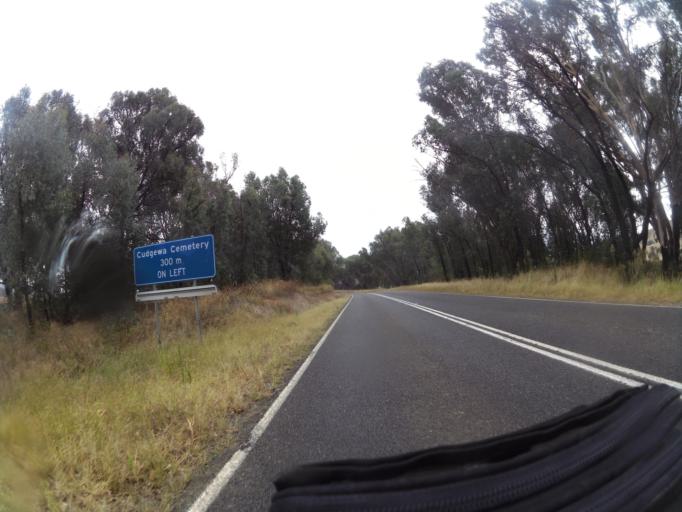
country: AU
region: New South Wales
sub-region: Greater Hume Shire
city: Holbrook
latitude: -36.2066
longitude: 147.7979
